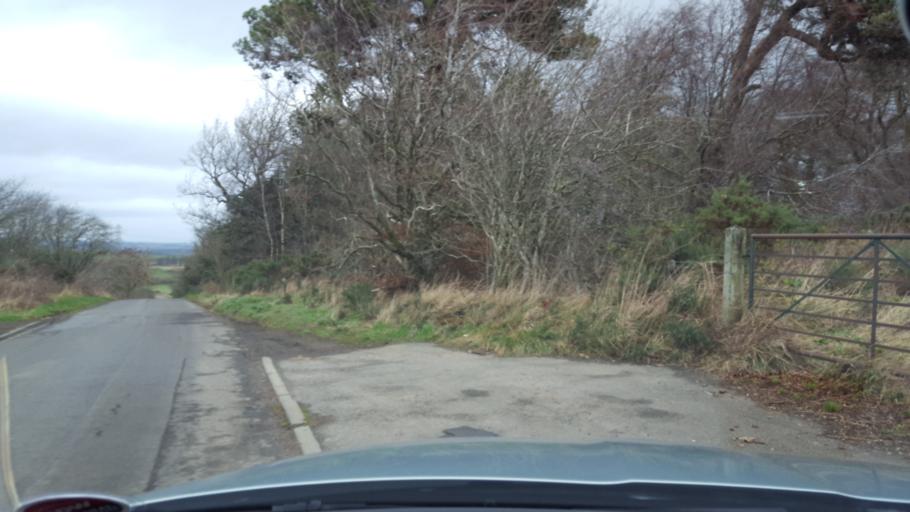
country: GB
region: Scotland
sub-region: West Lothian
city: Kirknewton
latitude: 55.8669
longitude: -3.4329
